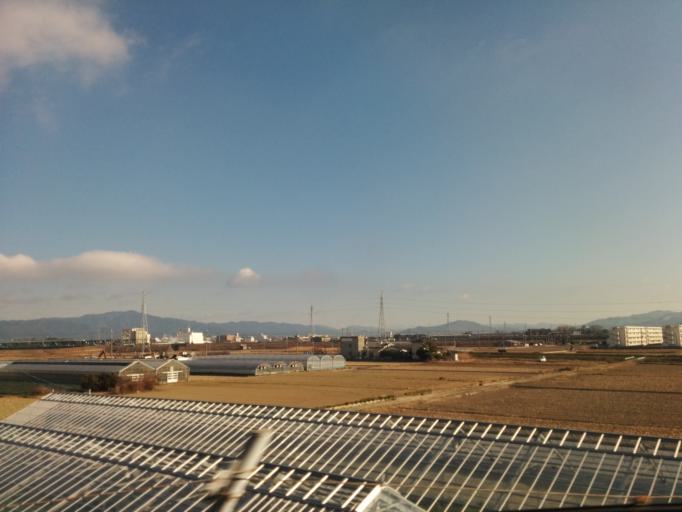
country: JP
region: Aichi
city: Kozakai-cho
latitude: 34.7844
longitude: 137.3614
